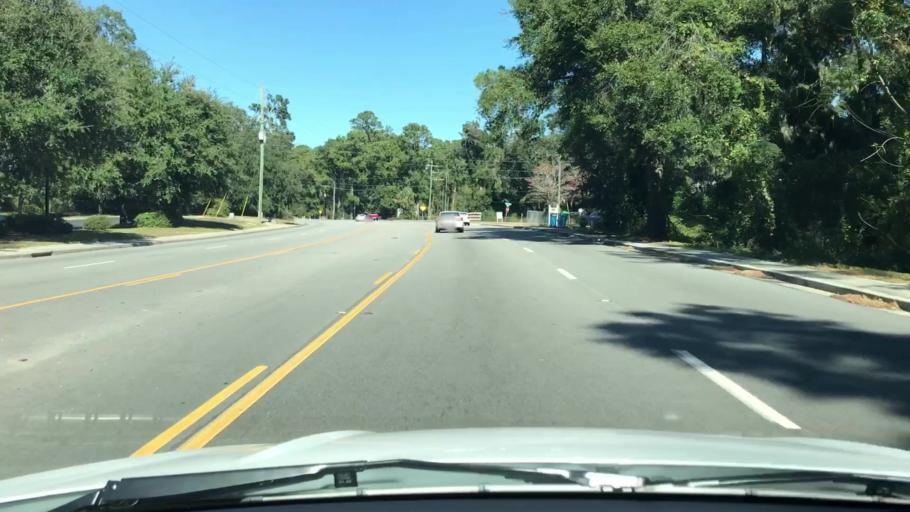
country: US
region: South Carolina
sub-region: Beaufort County
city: Burton
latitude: 32.4311
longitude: -80.7247
